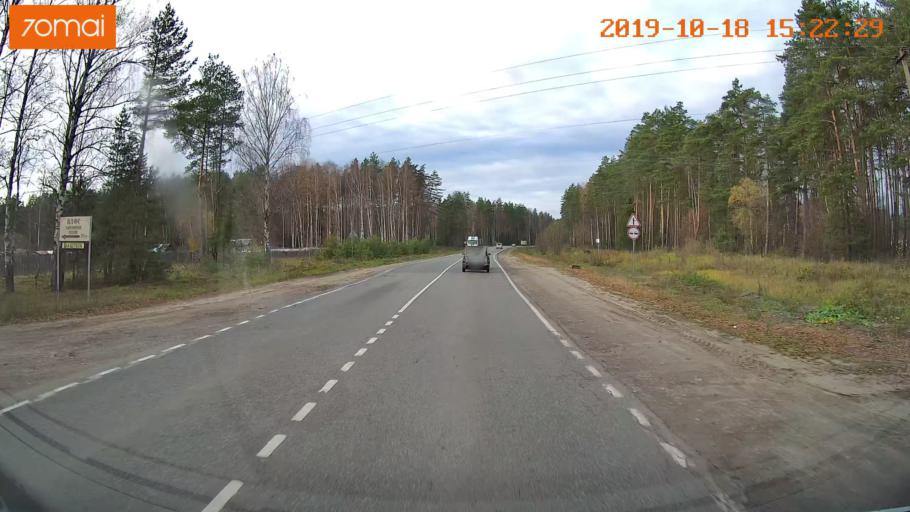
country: RU
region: Vladimir
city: Anopino
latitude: 55.7082
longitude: 40.7310
